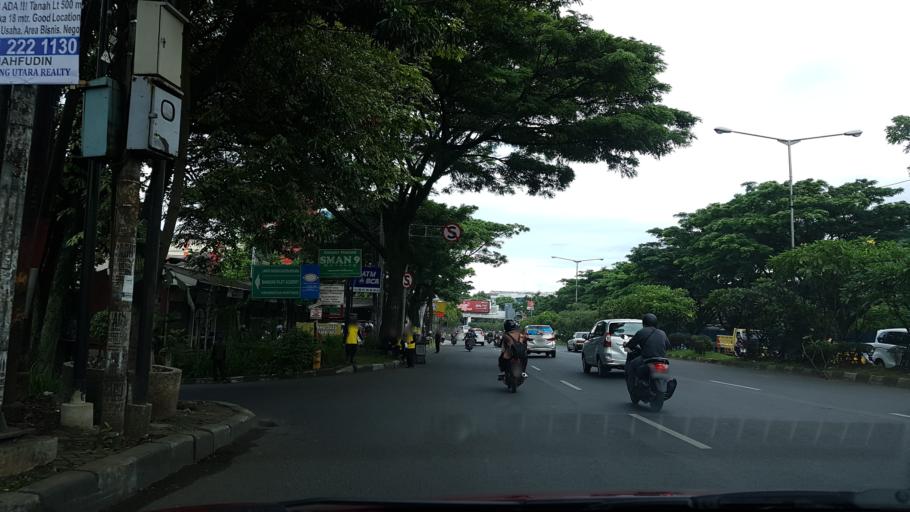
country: ID
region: West Java
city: Bandung
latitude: -6.8941
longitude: 107.5871
